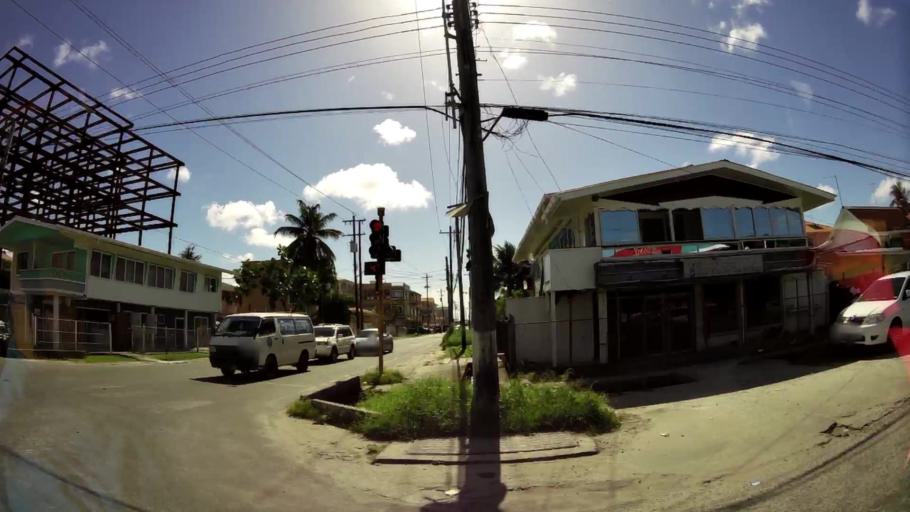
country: GY
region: Demerara-Mahaica
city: Georgetown
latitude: 6.8159
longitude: -58.1358
